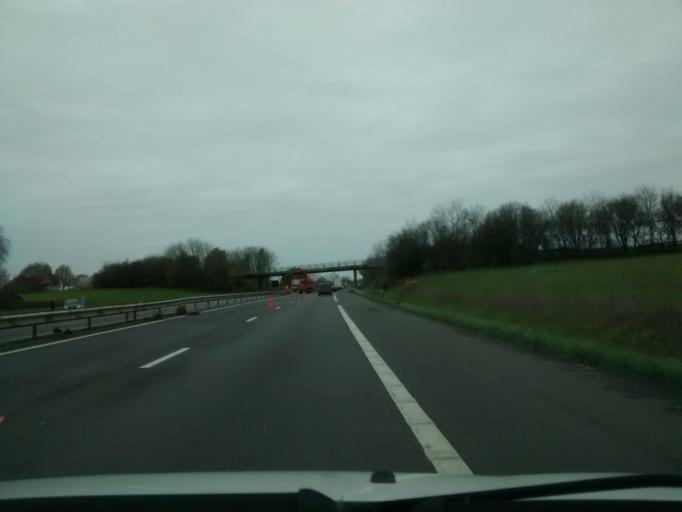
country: FR
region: Brittany
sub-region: Departement d'Ille-et-Vilaine
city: Louvigne-de-Bais
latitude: 48.0788
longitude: -1.3229
